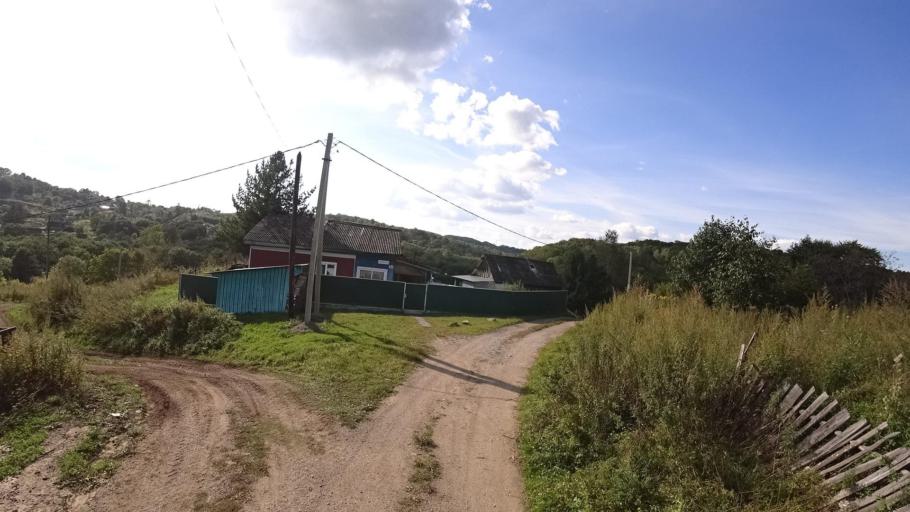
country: RU
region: Jewish Autonomous Oblast
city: Birakan
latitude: 49.0033
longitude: 131.7206
